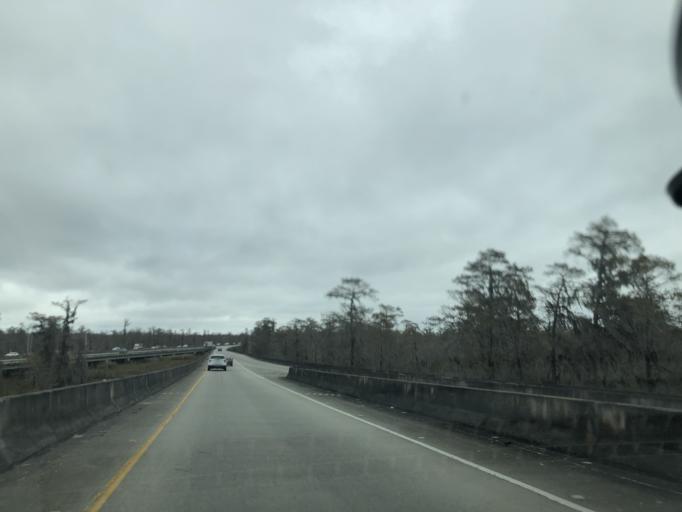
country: US
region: Louisiana
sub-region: Saint Charles Parish
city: Ama
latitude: 29.9774
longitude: -90.3151
